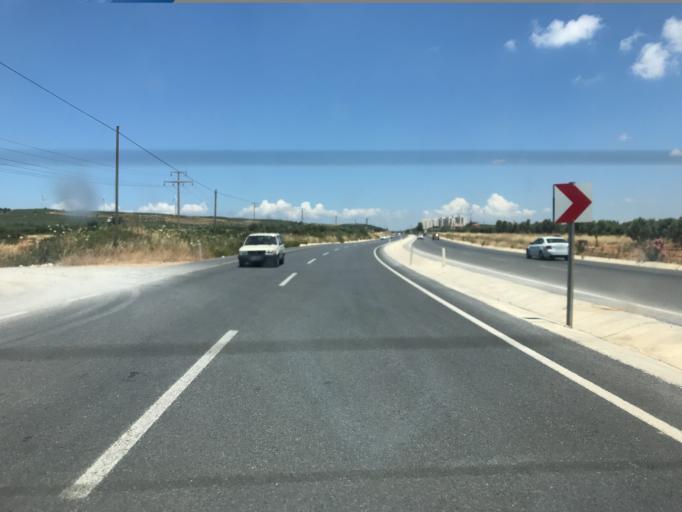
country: TR
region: Aydin
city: Akkoy
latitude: 37.4647
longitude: 27.3389
